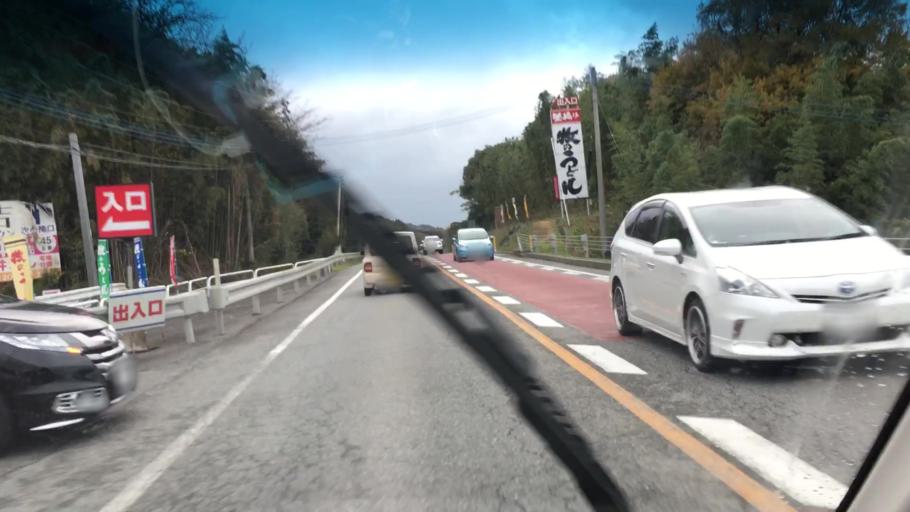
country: JP
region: Fukuoka
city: Maebaru-chuo
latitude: 33.5086
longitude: 130.1252
